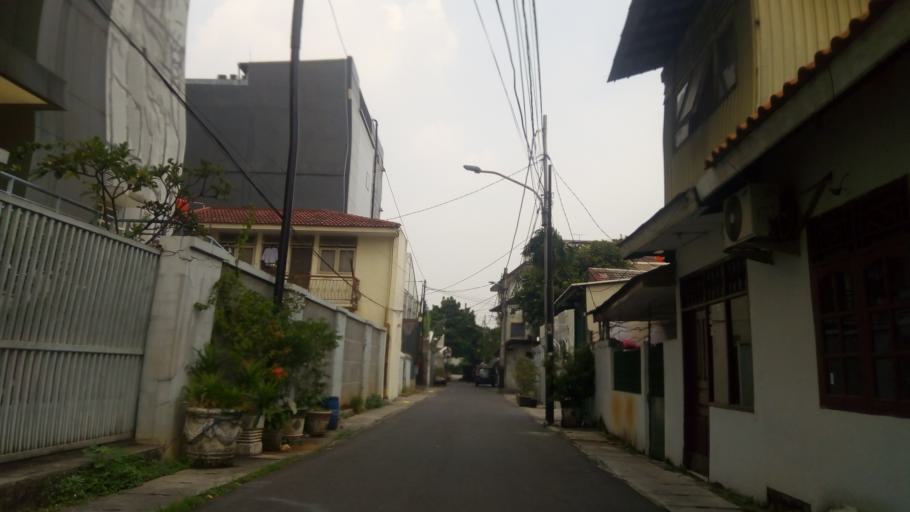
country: ID
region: Jakarta Raya
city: Jakarta
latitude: -6.1890
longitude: 106.8353
